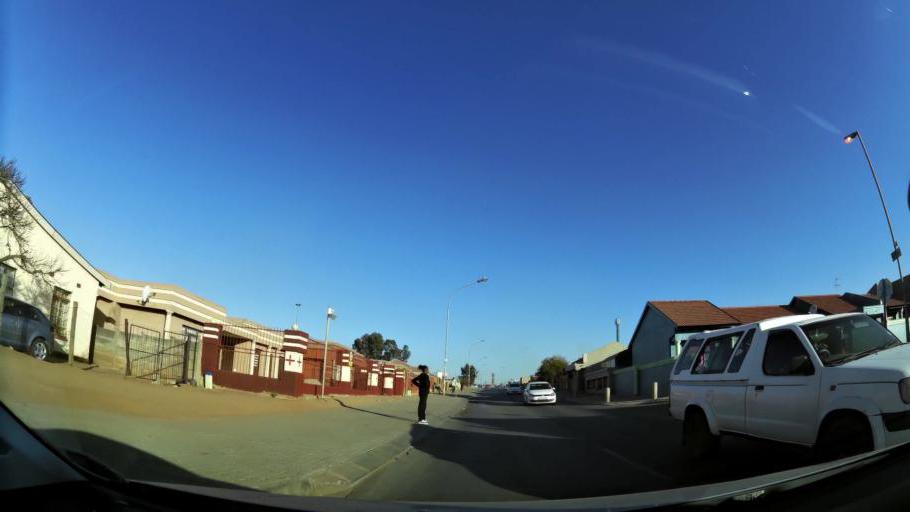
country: ZA
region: Gauteng
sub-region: Ekurhuleni Metropolitan Municipality
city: Tembisa
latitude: -26.0133
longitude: 28.2300
